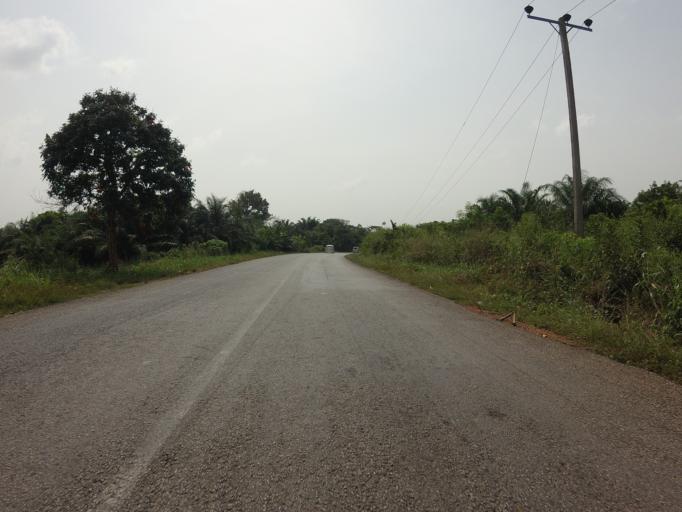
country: GH
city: Akropong
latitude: 6.2706
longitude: 0.1359
